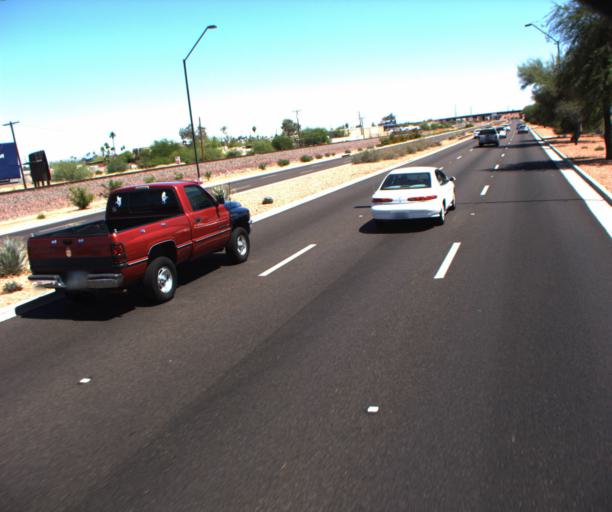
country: US
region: Arizona
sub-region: Maricopa County
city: Peoria
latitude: 33.5718
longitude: -112.2263
